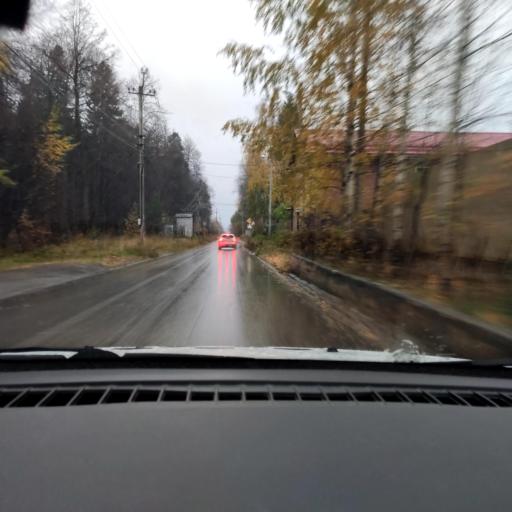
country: RU
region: Perm
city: Kondratovo
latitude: 58.0533
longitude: 56.1221
